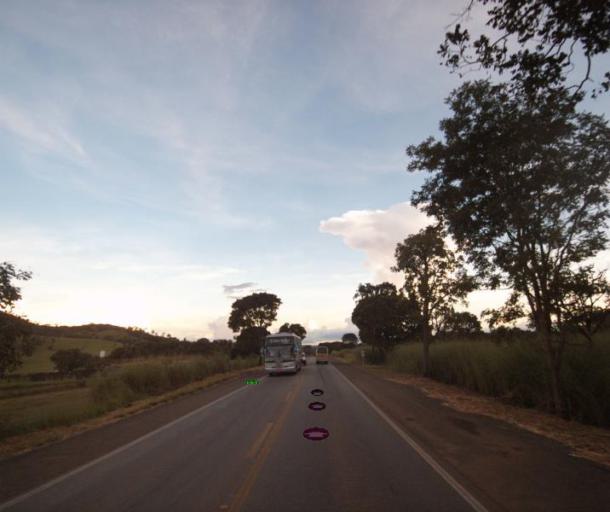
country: BR
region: Goias
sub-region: Uruacu
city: Uruacu
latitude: -14.4011
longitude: -49.1576
